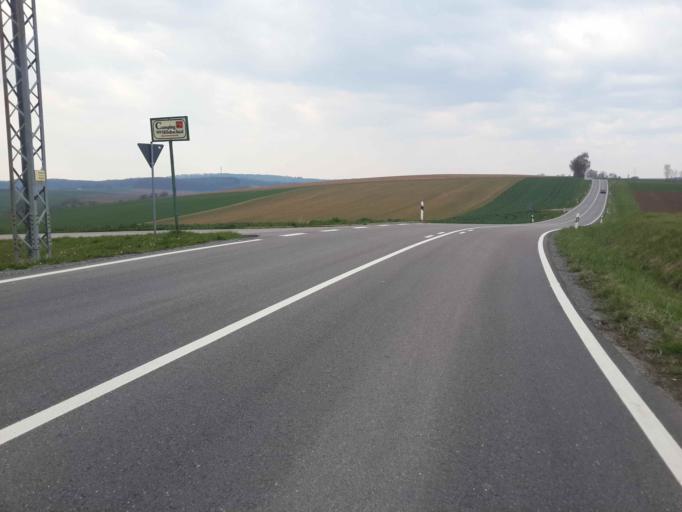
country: DE
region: Baden-Wuerttemberg
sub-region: Regierungsbezirk Stuttgart
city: Eppingen
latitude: 49.1790
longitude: 8.8742
